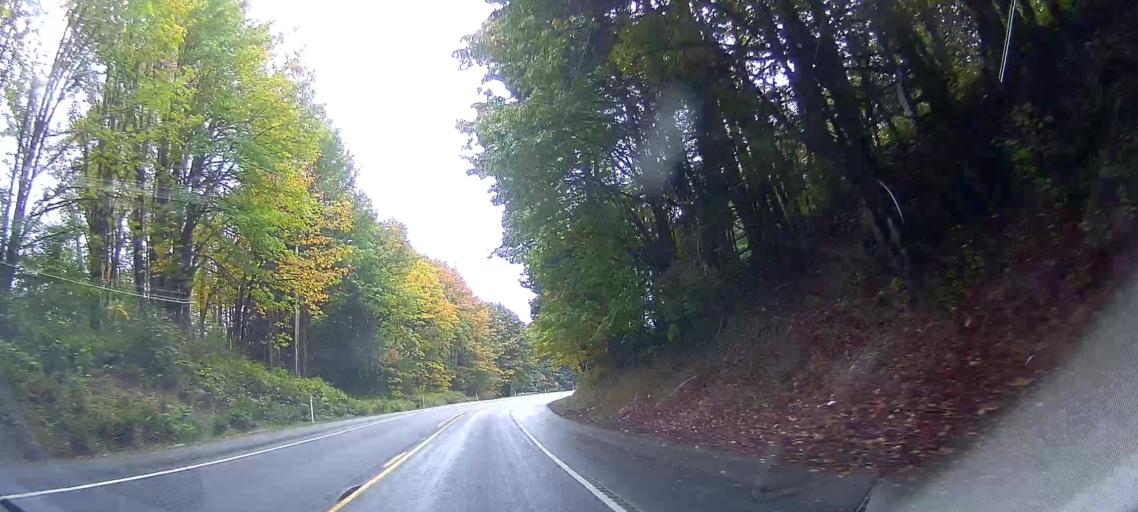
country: US
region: Washington
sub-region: Snohomish County
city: Darrington
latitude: 48.5407
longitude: -121.8042
